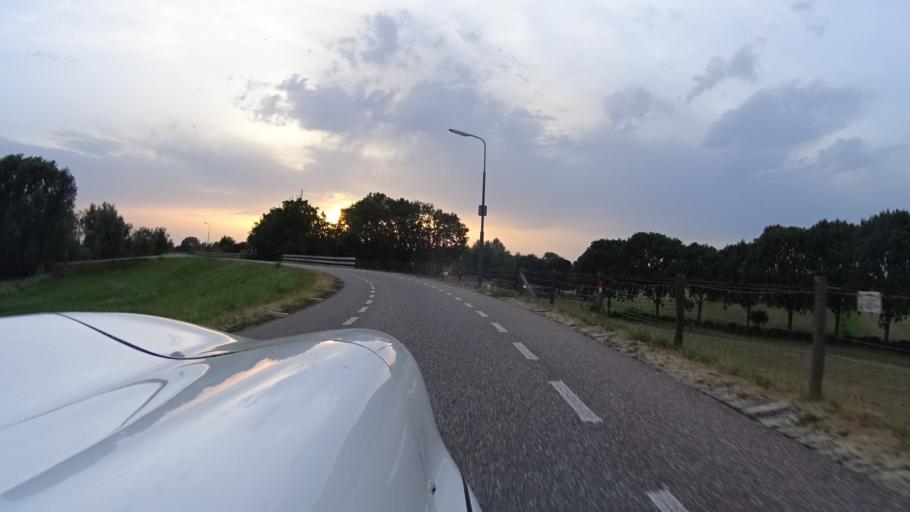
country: NL
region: Utrecht
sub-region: Gemeente Lopik
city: Lopik
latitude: 51.9657
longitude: 4.9505
